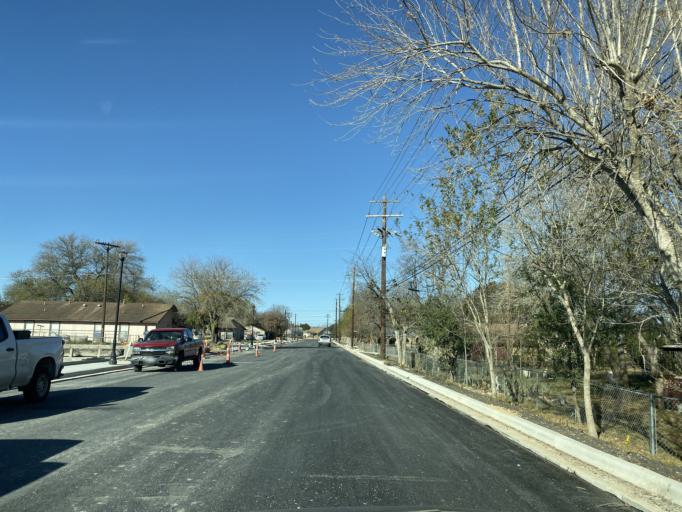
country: US
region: Texas
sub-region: Hays County
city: Kyle
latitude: 29.9961
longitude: -97.8758
